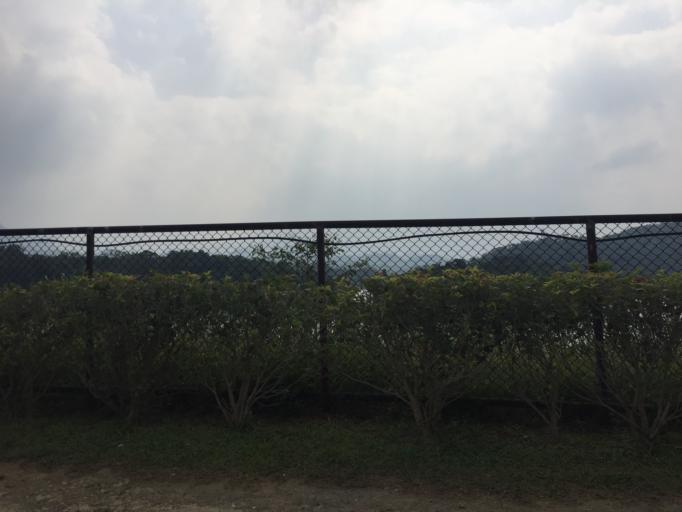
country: TW
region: Taiwan
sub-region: Hsinchu
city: Hsinchu
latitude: 24.6806
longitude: 120.9844
